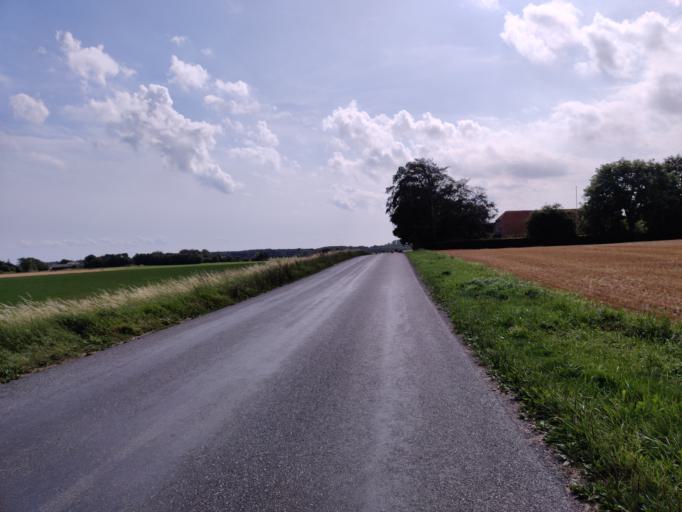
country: DK
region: Zealand
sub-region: Guldborgsund Kommune
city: Nykobing Falster
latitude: 54.6593
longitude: 11.8891
